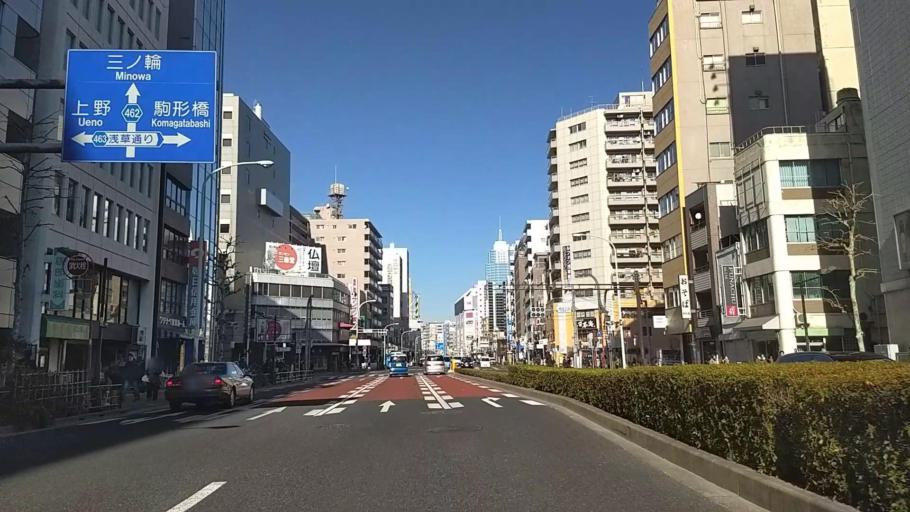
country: JP
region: Tokyo
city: Tokyo
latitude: 35.7090
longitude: 139.7912
